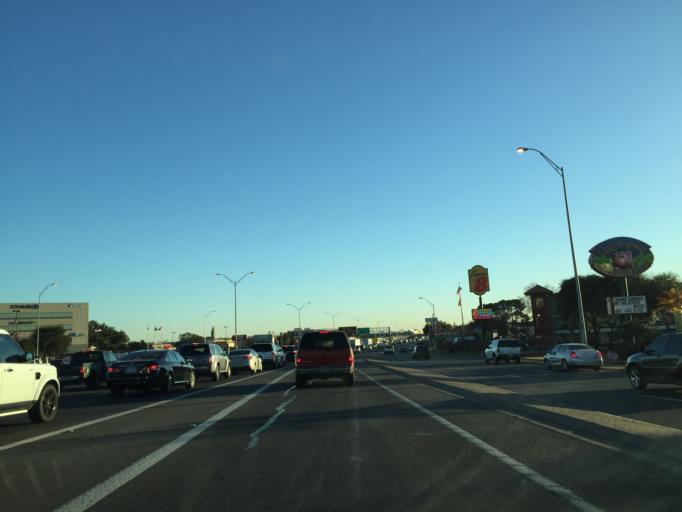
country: US
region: Texas
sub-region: Travis County
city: Austin
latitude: 30.3164
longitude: -97.7078
